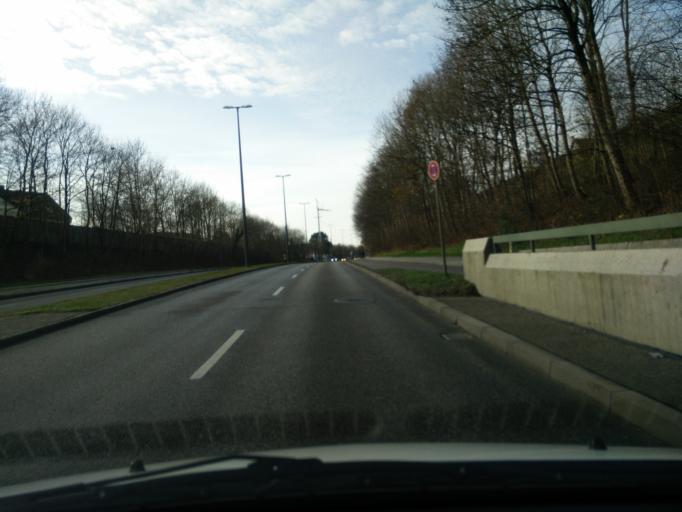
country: DE
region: Bavaria
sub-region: Upper Bavaria
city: Karlsfeld
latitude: 48.1777
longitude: 11.4717
